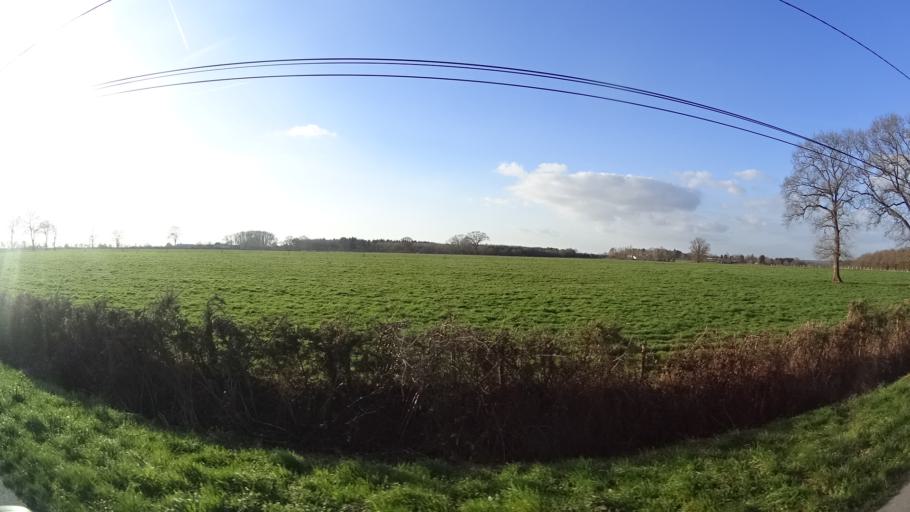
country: FR
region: Pays de la Loire
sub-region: Departement de la Loire-Atlantique
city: Plesse
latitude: 47.5202
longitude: -1.8863
